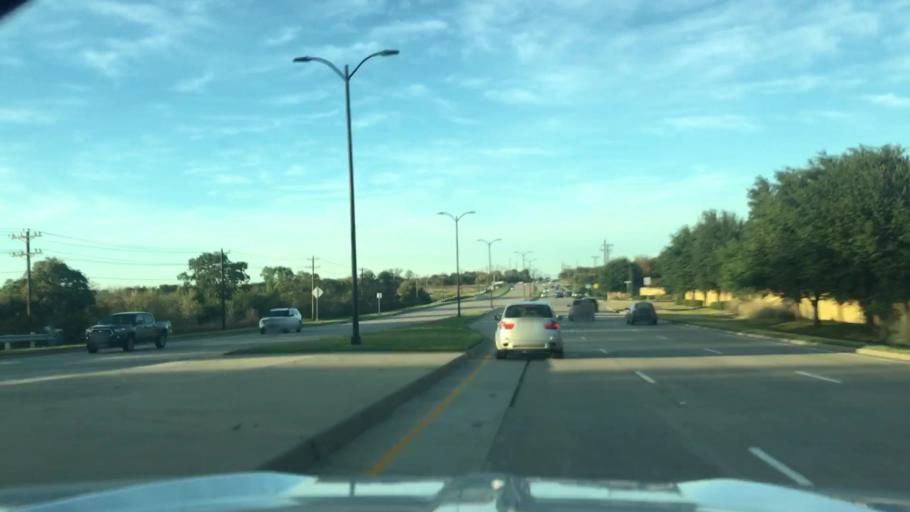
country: US
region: Texas
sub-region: Collin County
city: Frisco
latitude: 33.1762
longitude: -96.8030
